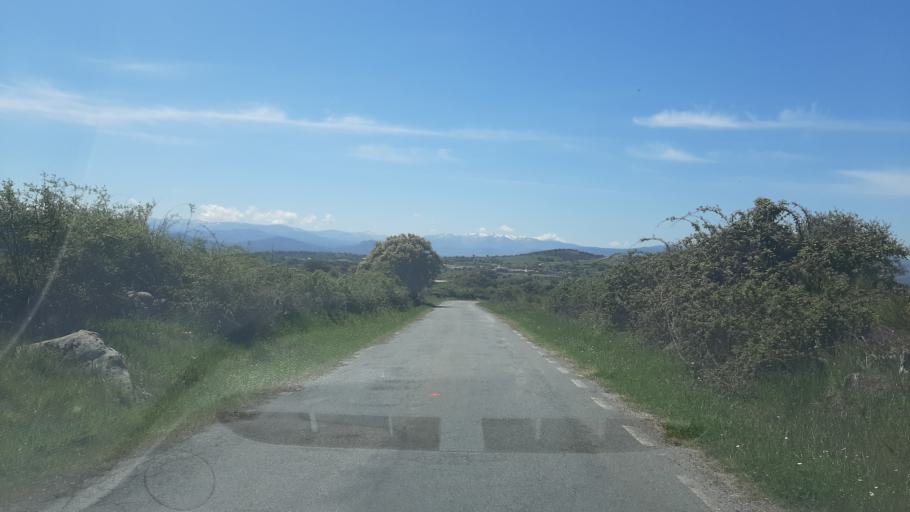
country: ES
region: Castille and Leon
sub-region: Provincia de Avila
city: Narrillos del Alamo
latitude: 40.5537
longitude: -5.4416
